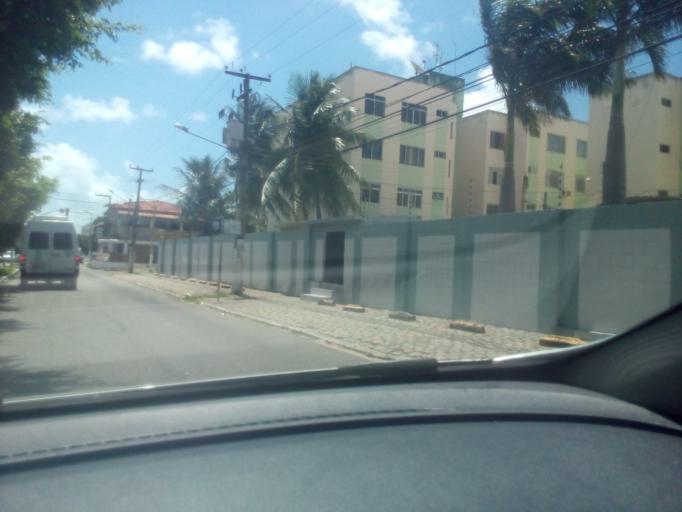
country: BR
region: Rio Grande do Norte
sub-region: Parnamirim
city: Parnamirim
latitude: -5.8803
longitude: -35.2066
